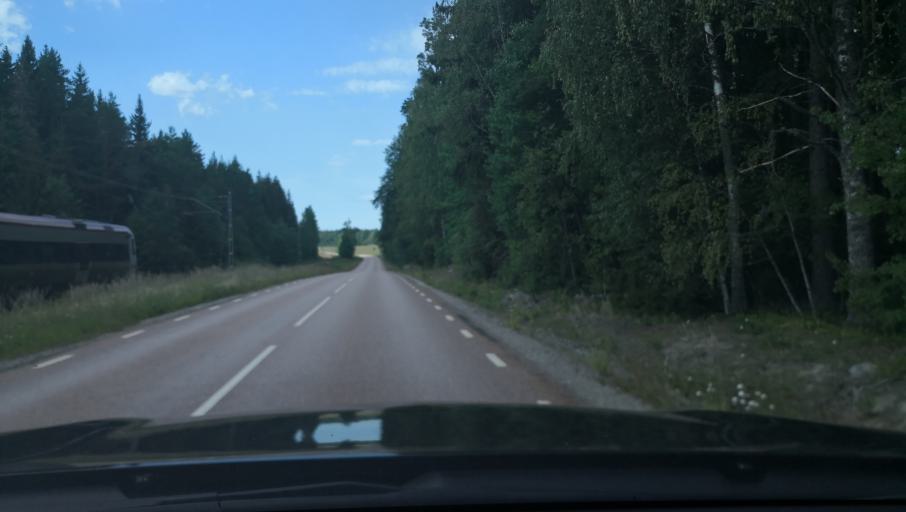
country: SE
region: Vaestmanland
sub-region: Surahammars Kommun
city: Ramnas
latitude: 59.8350
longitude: 16.1307
